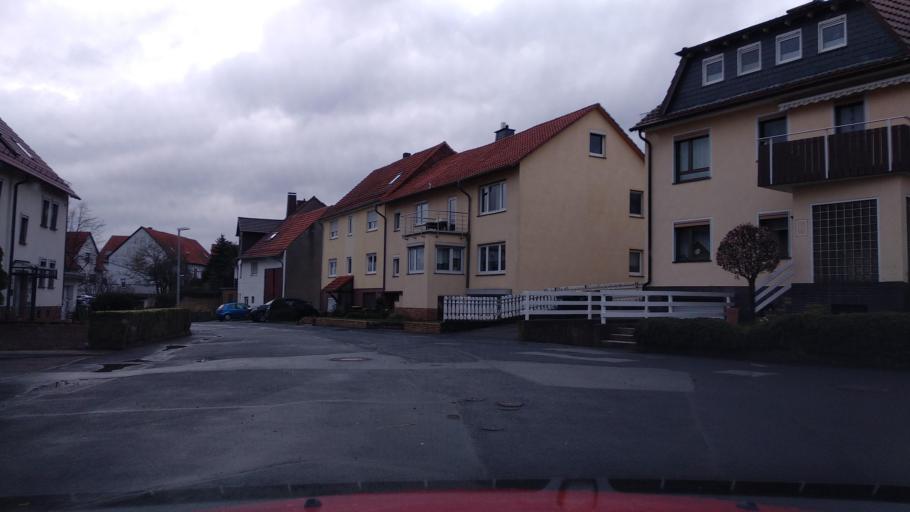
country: DE
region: Hesse
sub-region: Regierungsbezirk Kassel
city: Calden
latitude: 51.3640
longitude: 9.3933
